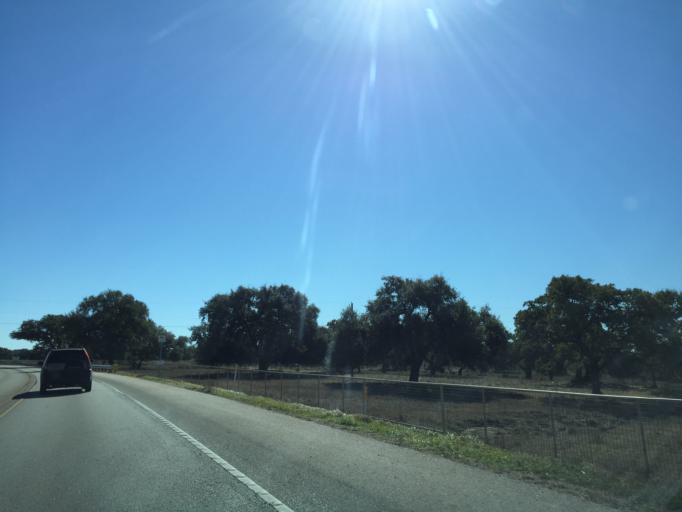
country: US
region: Texas
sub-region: Comal County
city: Canyon Lake
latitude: 29.7794
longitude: -98.3164
